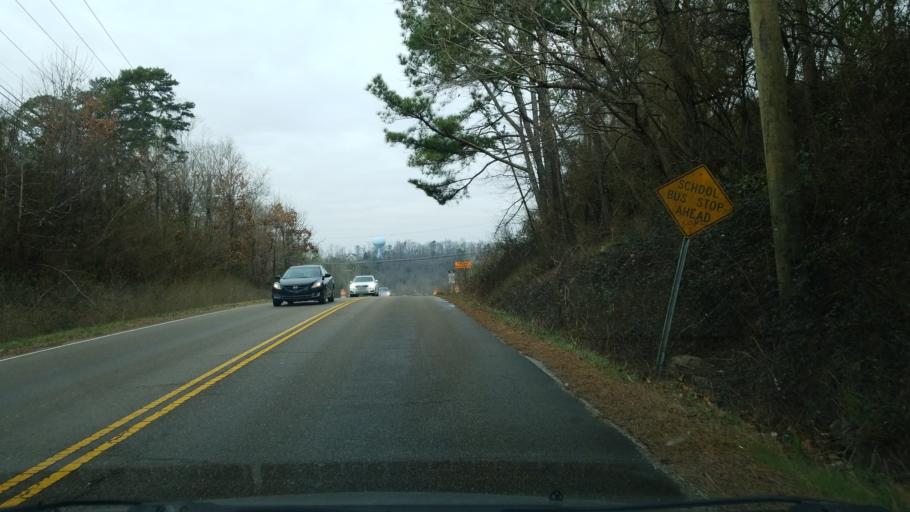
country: US
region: Tennessee
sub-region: Hamilton County
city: East Brainerd
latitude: 35.0024
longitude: -85.1145
